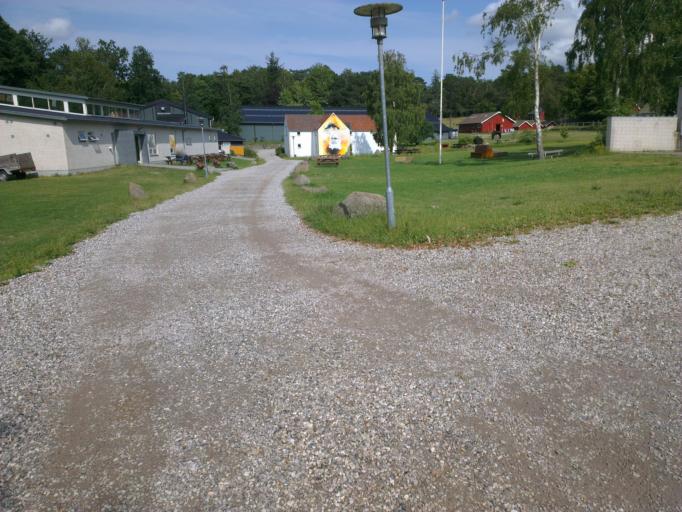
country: DK
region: Capital Region
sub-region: Frederikssund Kommune
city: Jaegerspris
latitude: 55.9074
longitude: 11.9173
